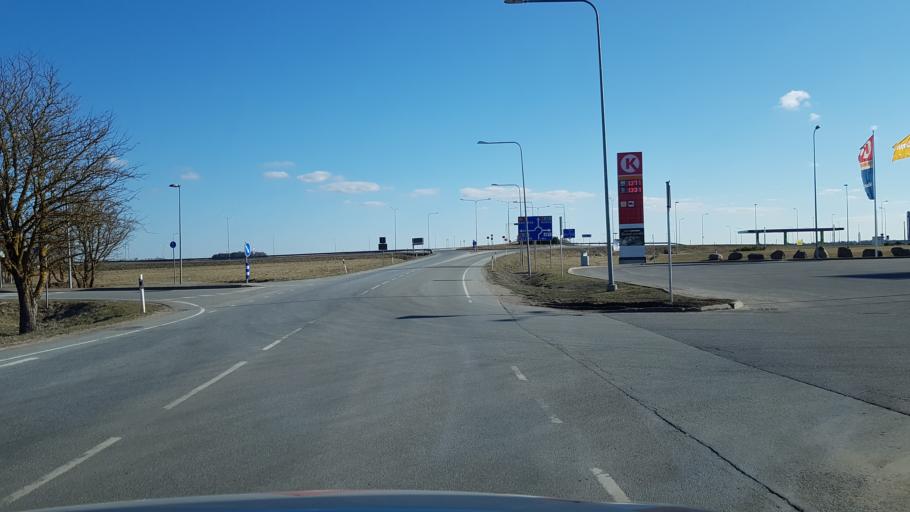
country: EE
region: Laeaene-Virumaa
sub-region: Haljala vald
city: Haljala
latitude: 59.4268
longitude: 26.2696
